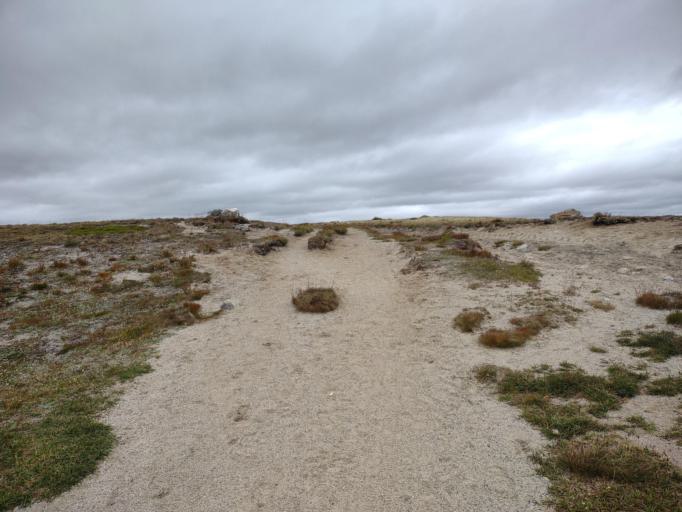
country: NO
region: Hordaland
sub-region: Eidfjord
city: Eidfjord
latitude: 60.2474
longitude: 7.5464
